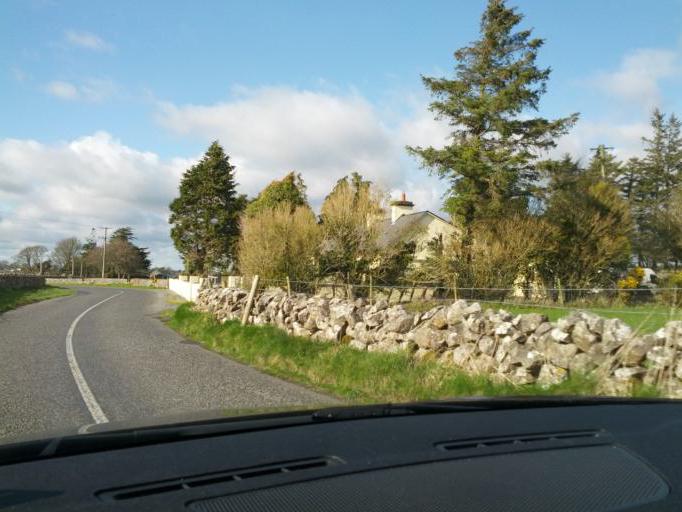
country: IE
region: Connaught
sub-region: County Galway
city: Athenry
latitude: 53.4244
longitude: -8.5723
